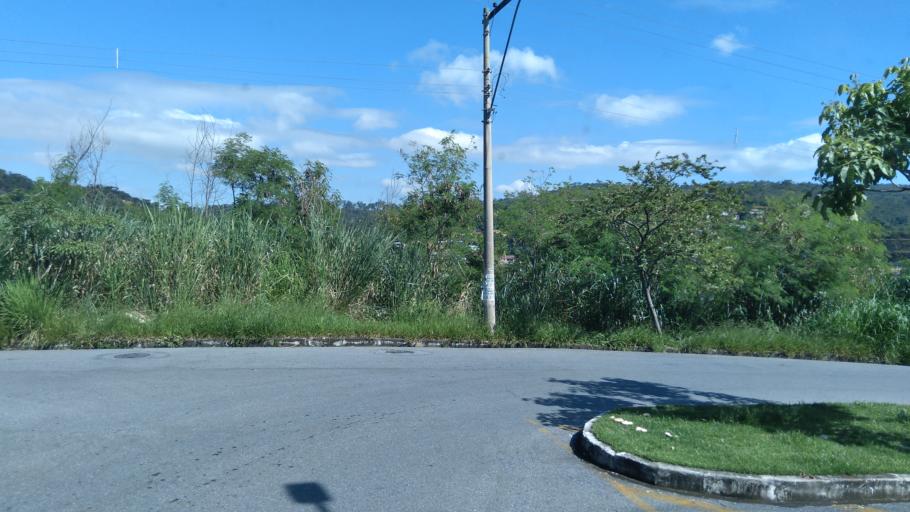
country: BR
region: Minas Gerais
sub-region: Santa Luzia
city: Santa Luzia
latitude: -19.8243
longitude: -43.8996
